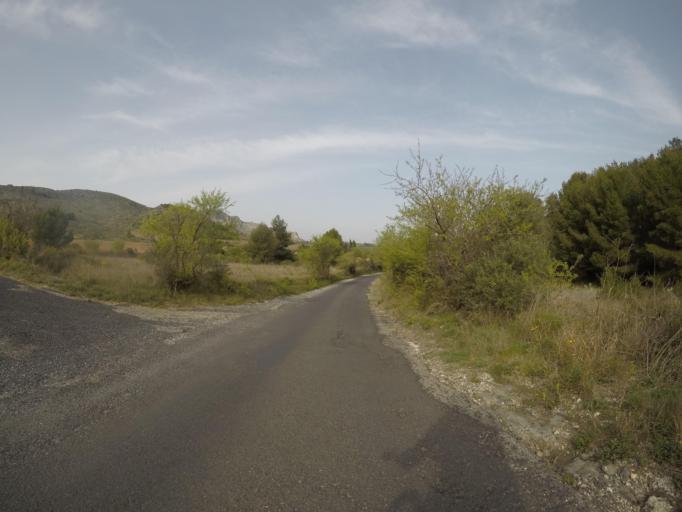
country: FR
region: Languedoc-Roussillon
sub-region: Departement des Pyrenees-Orientales
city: Baixas
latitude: 42.7715
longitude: 2.7997
